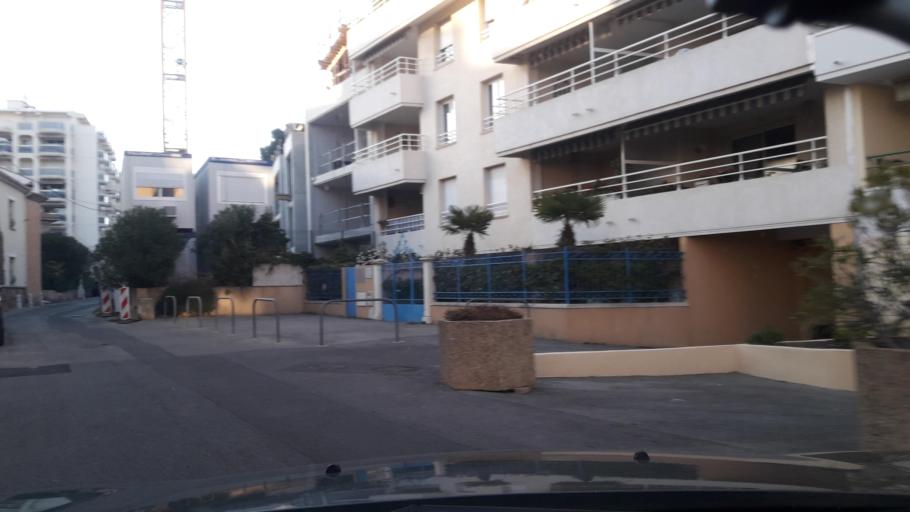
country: FR
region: Provence-Alpes-Cote d'Azur
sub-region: Departement du Var
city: Saint-Raphael
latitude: 43.4197
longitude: 6.7726
